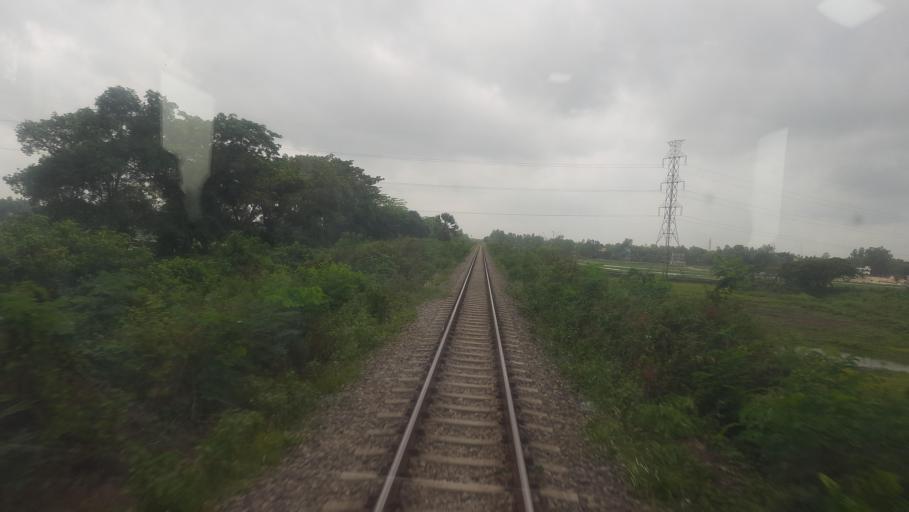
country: BD
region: Dhaka
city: Bhairab Bazar
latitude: 24.0411
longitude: 90.9643
